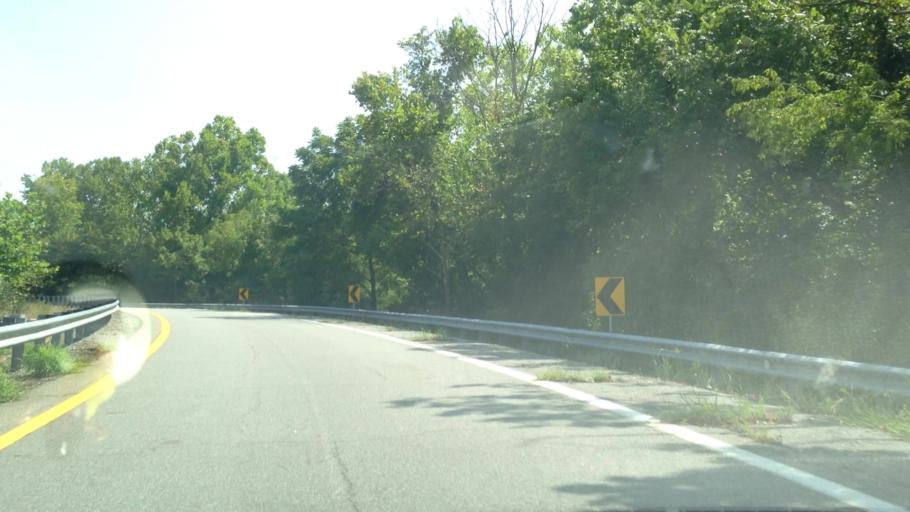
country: US
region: Virginia
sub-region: Henry County
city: Stanleytown
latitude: 36.7375
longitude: -79.9387
